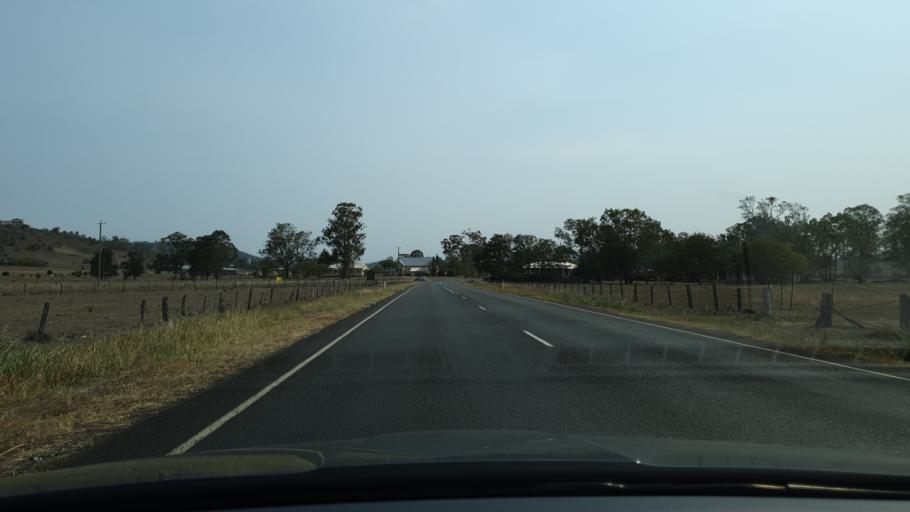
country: AU
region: Queensland
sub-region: Ipswich
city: Deebing Heights
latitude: -28.0111
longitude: 152.6775
